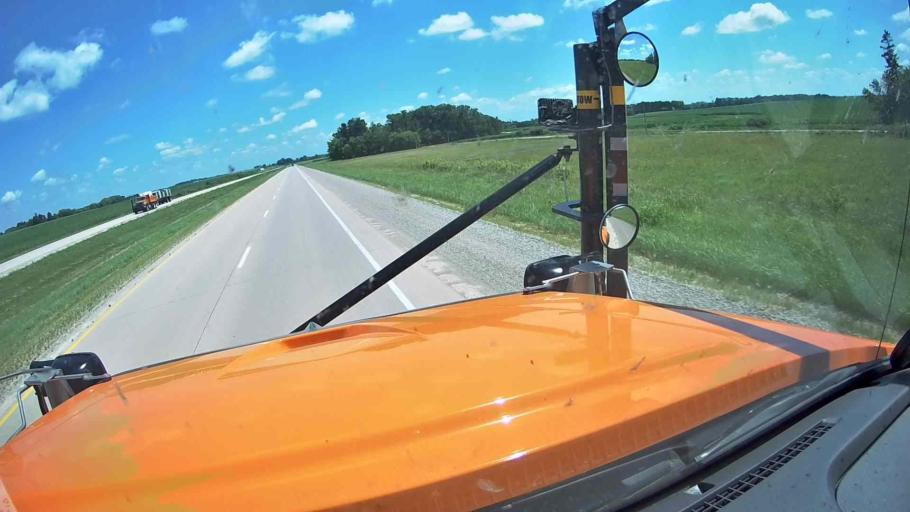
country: US
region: Iowa
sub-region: Floyd County
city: Nora Springs
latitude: 43.1162
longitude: -92.9746
